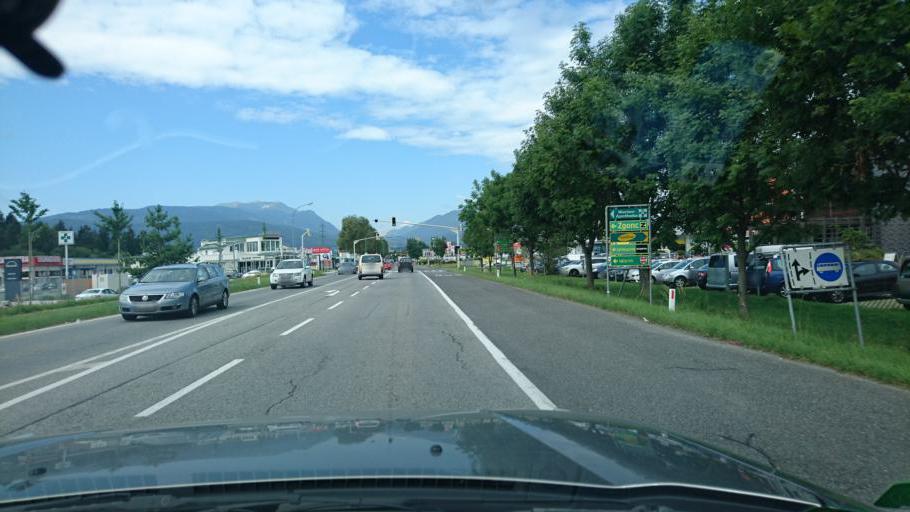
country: AT
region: Carinthia
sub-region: Villach Stadt
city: Villach
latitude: 46.6043
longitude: 13.8702
